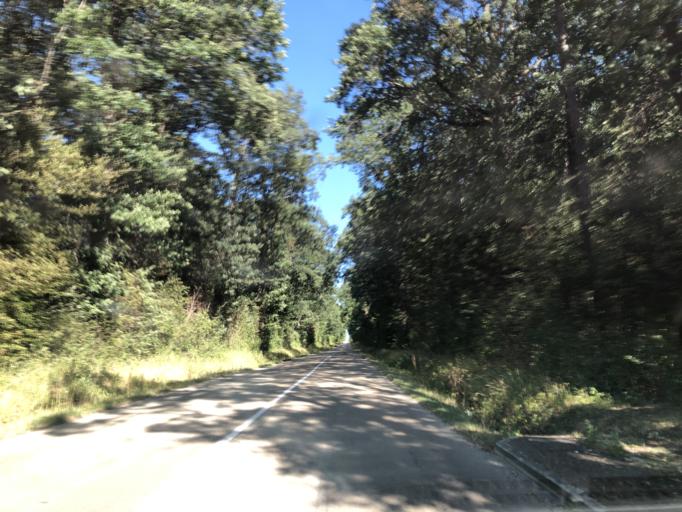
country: FR
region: Bourgogne
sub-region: Departement de l'Yonne
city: Gurgy
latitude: 47.8992
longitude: 3.5659
